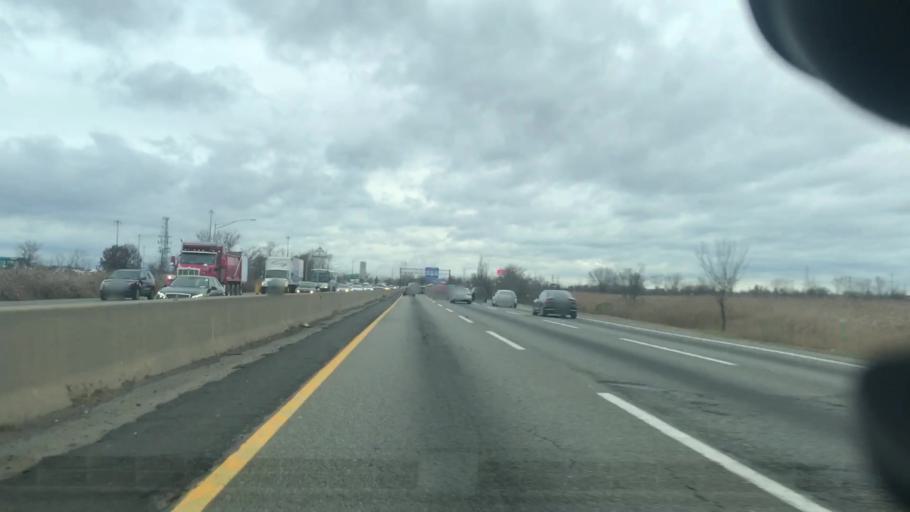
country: US
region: New Jersey
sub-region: Hudson County
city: North Bergen
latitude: 40.8196
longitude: -74.0277
